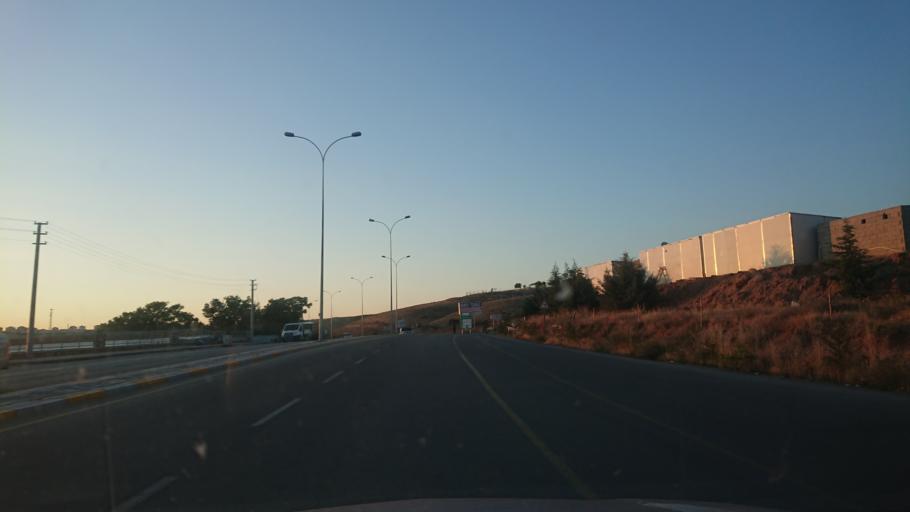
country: TR
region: Aksaray
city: Aksaray
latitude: 38.4066
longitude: 34.0126
